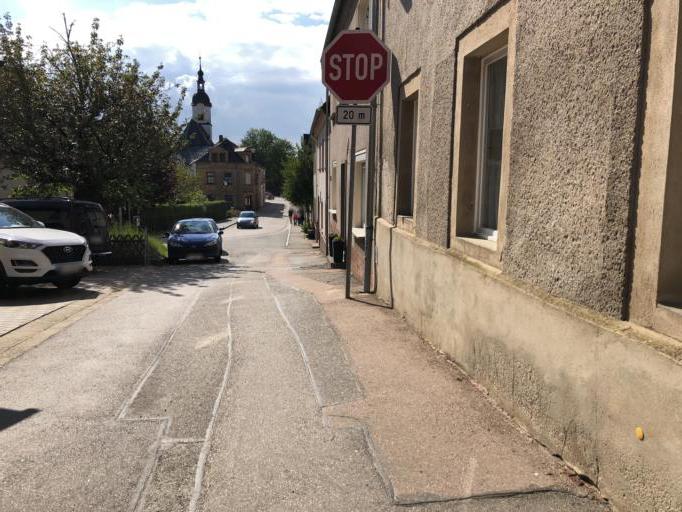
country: DE
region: Saxony
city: Wechselburg
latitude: 51.0051
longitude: 12.7758
